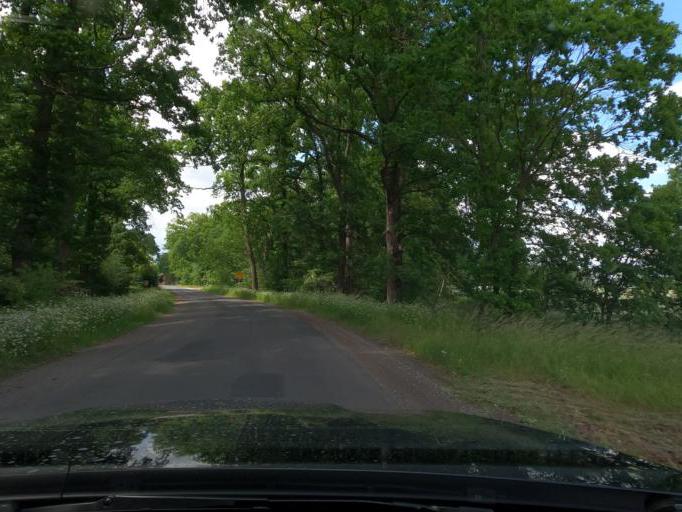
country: DE
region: Lower Saxony
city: Schwarmstedt
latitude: 52.6580
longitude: 9.6214
